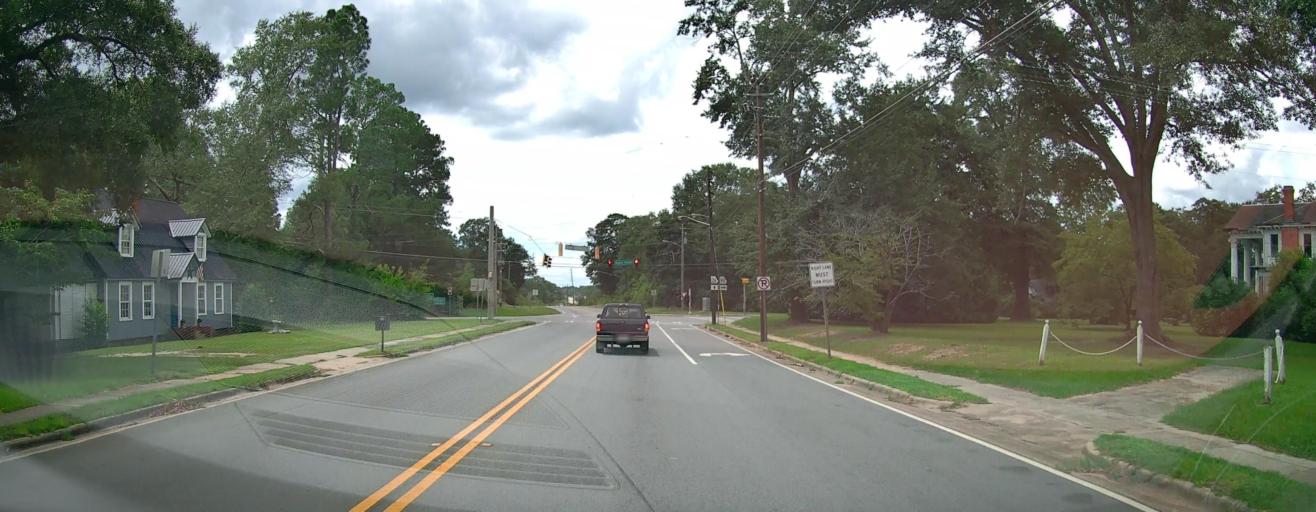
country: US
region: Georgia
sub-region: Macon County
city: Montezuma
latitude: 32.2935
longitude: -84.0307
